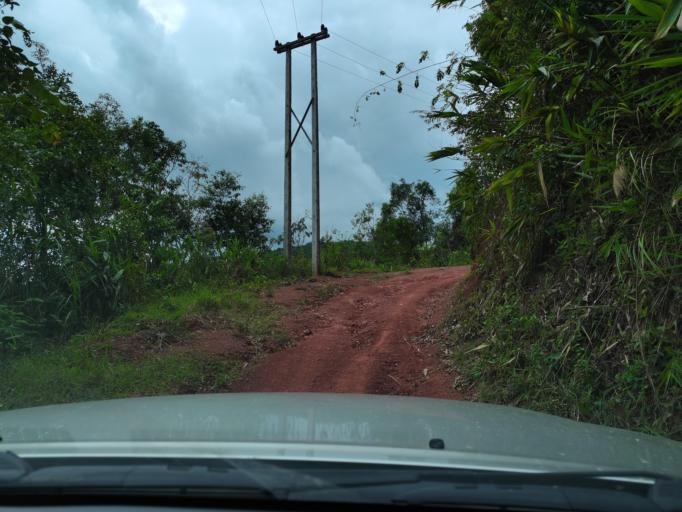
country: LA
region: Loungnamtha
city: Muang Nale
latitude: 20.5054
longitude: 101.0837
